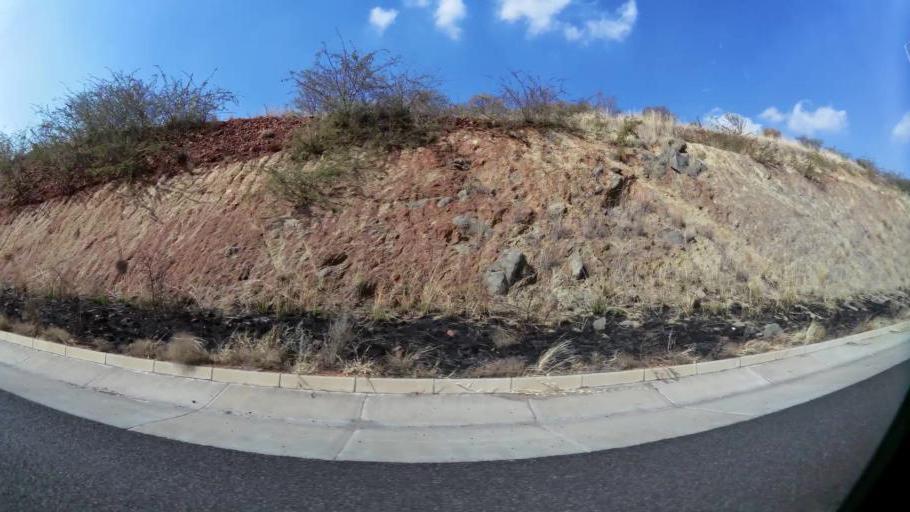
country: ZA
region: North-West
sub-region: Bojanala Platinum District Municipality
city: Rustenburg
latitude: -25.5701
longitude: 27.1404
